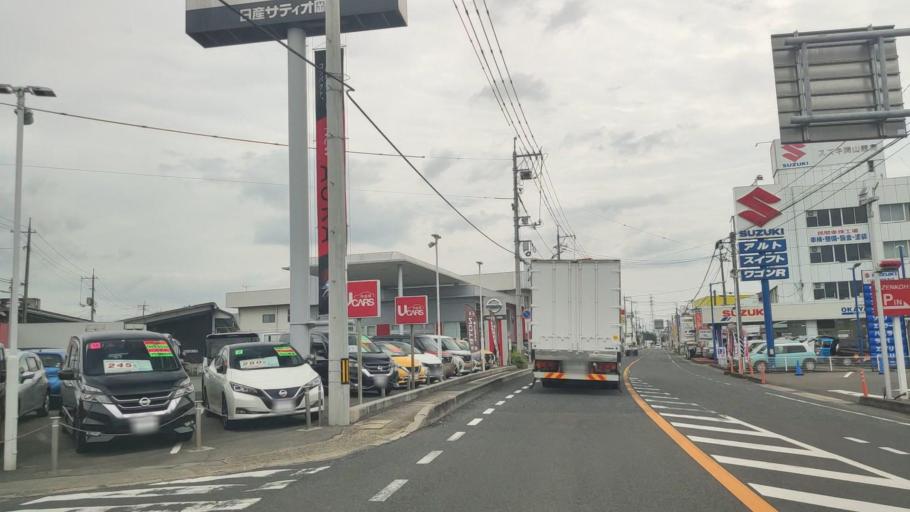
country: JP
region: Okayama
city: Tsuyama
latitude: 35.0578
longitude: 133.9822
